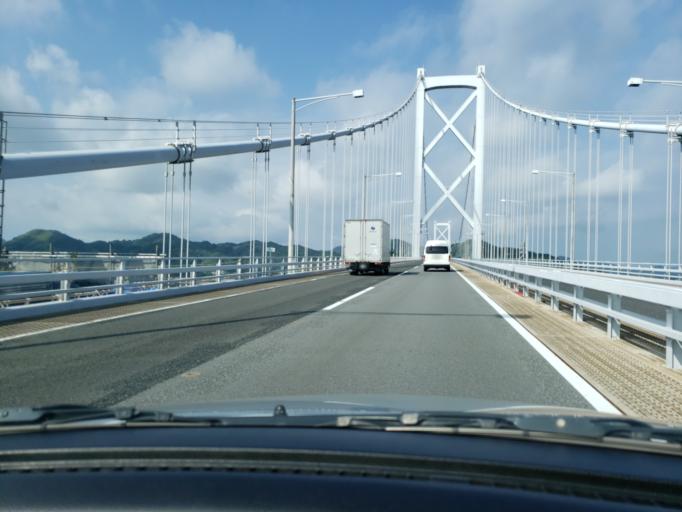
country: JP
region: Hiroshima
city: Onomichi
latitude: 34.3597
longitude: 133.1863
